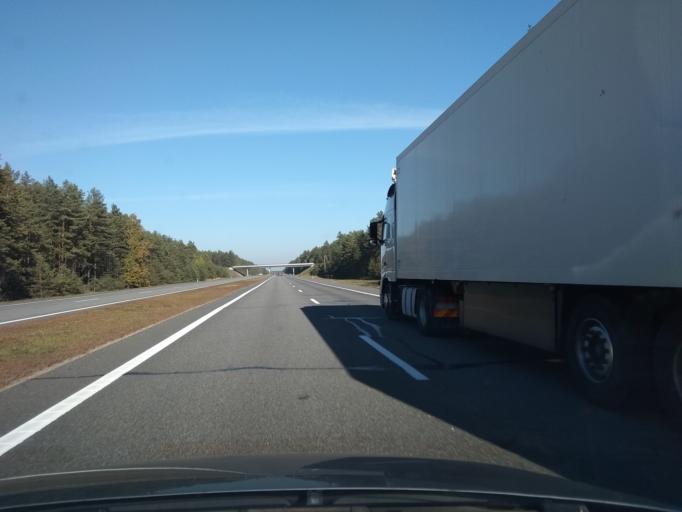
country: BY
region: Brest
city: Baranovichi
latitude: 52.9958
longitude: 25.7607
